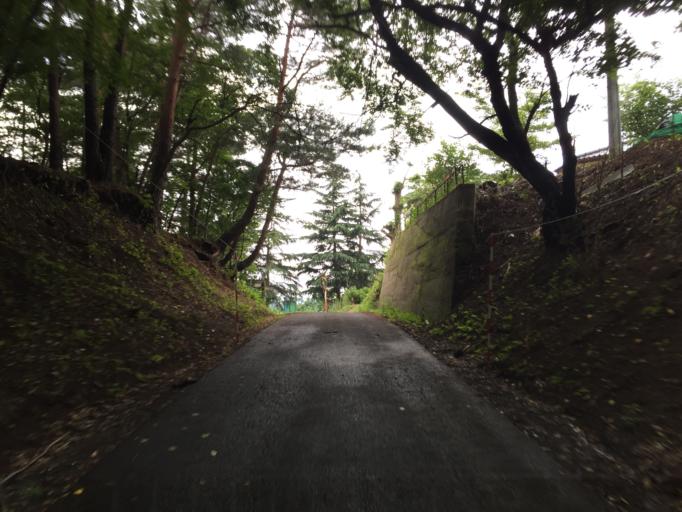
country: JP
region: Fukushima
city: Fukushima-shi
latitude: 37.7314
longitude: 140.4880
